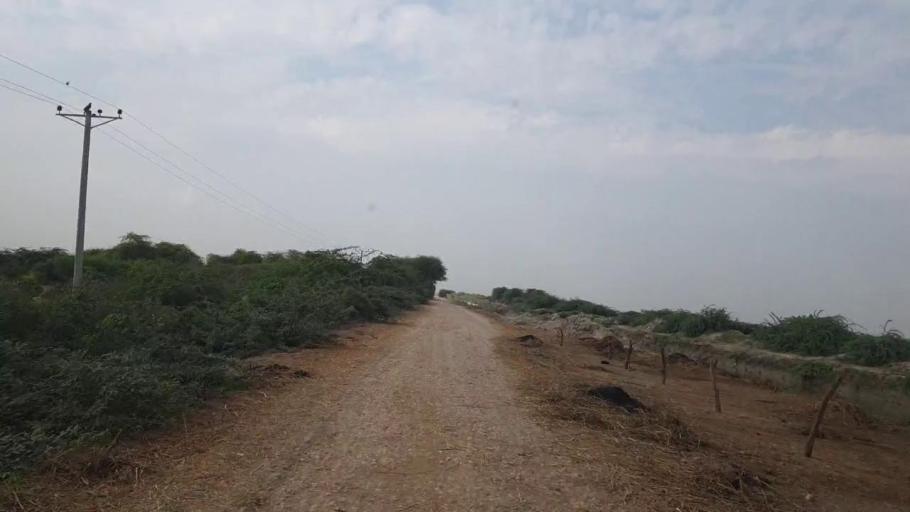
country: PK
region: Sindh
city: Kario
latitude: 24.6215
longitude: 68.5813
